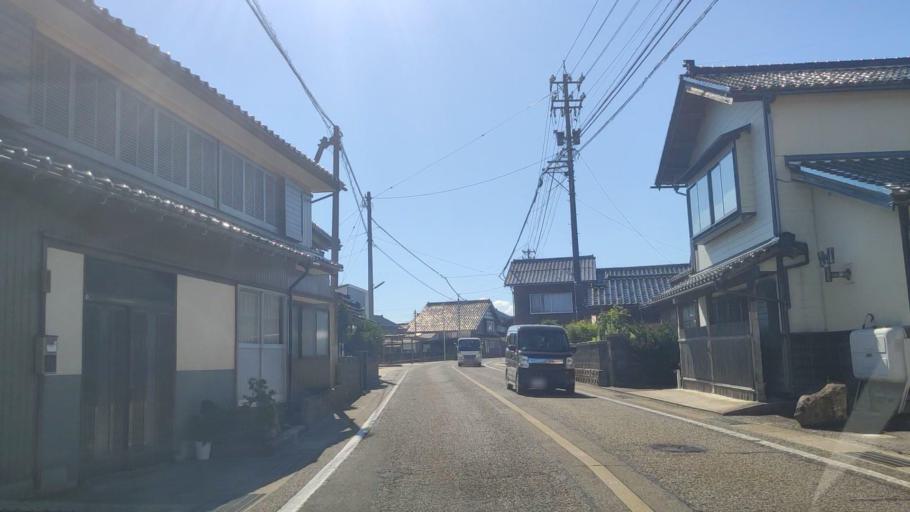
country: JP
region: Ishikawa
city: Nanao
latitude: 37.4433
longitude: 137.2851
